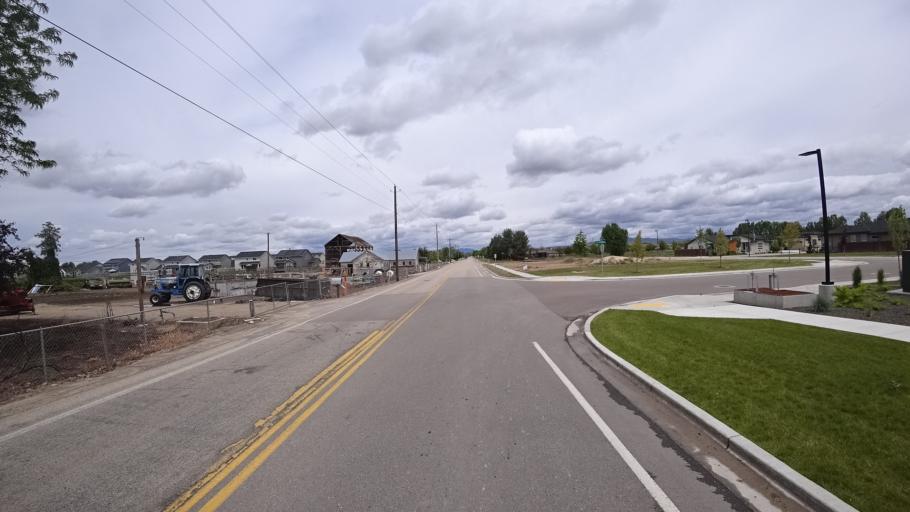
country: US
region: Idaho
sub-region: Ada County
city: Eagle
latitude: 43.6963
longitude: -116.4037
